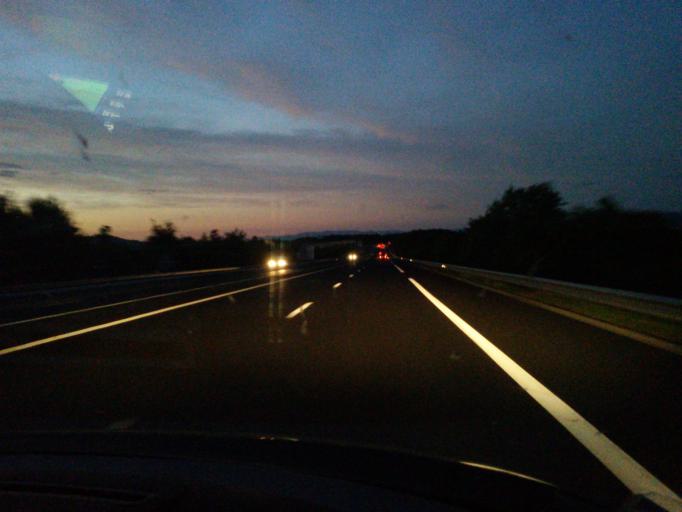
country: FR
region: Auvergne
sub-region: Departement de la Haute-Loire
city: Lempdes-sur-Allagnon
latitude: 45.3478
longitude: 3.2772
